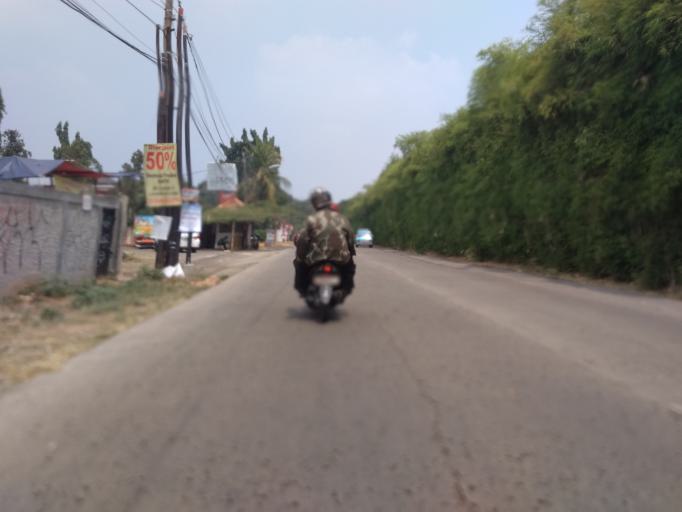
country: ID
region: West Java
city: Pamulang
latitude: -6.3176
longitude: 106.7892
